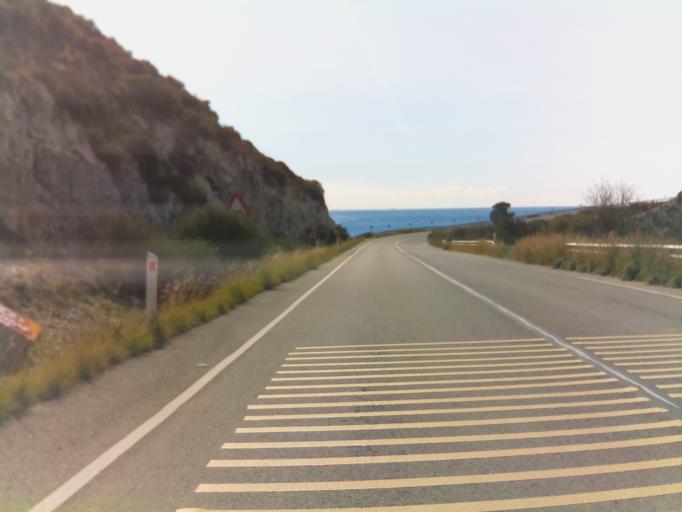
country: CY
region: Limassol
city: Pissouri
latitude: 34.6603
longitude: 32.6520
